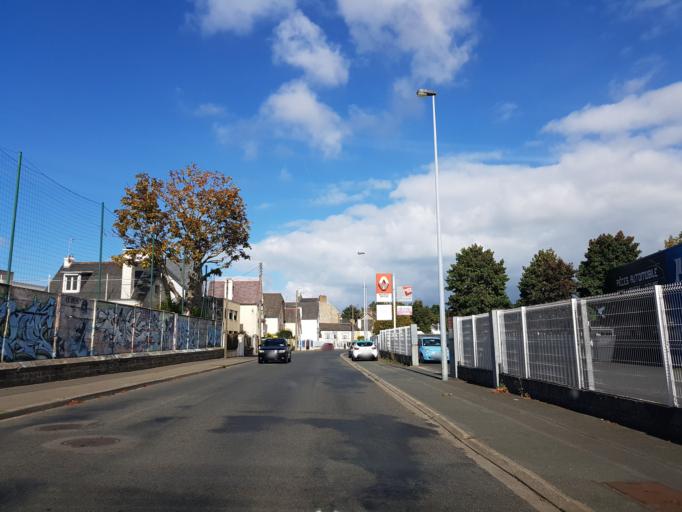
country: FR
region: Brittany
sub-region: Departement des Cotes-d'Armor
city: Saint-Brieuc
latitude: 48.5096
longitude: -2.7426
